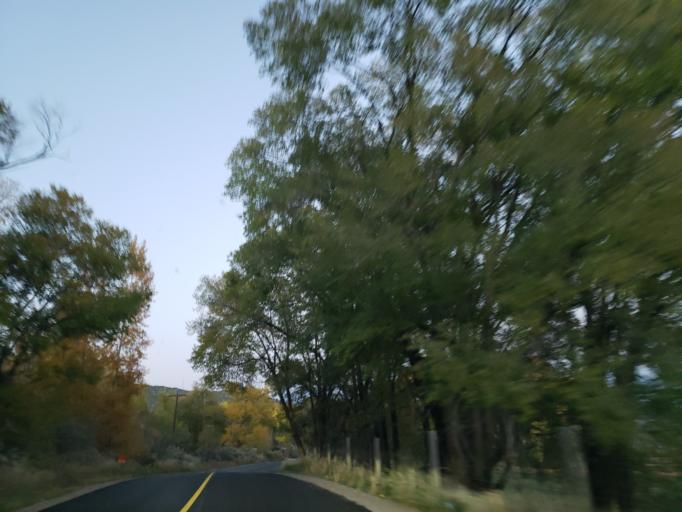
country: US
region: Colorado
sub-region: Garfield County
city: New Castle
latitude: 39.5575
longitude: -107.5864
